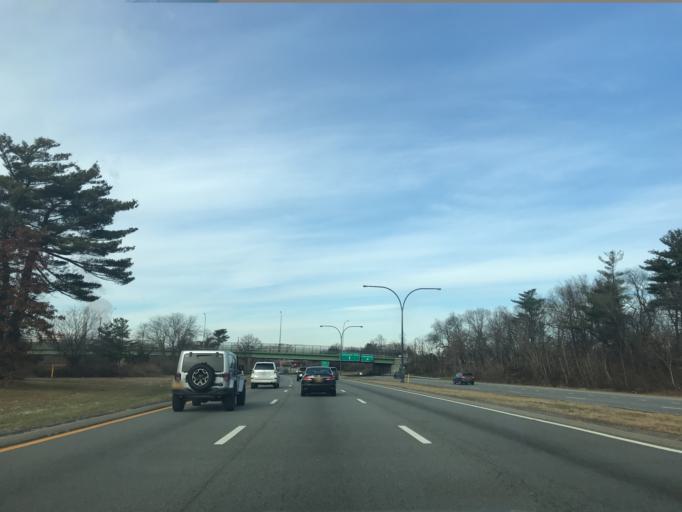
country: US
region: New York
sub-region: Nassau County
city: East Garden City
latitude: 40.7279
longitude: -73.5804
